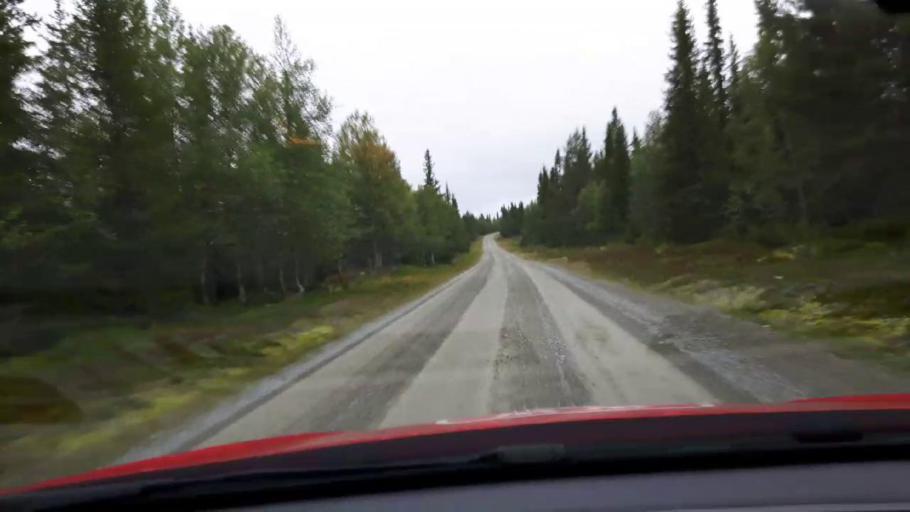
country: SE
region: Jaemtland
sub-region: Bergs Kommun
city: Hoverberg
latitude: 62.8627
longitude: 13.9474
